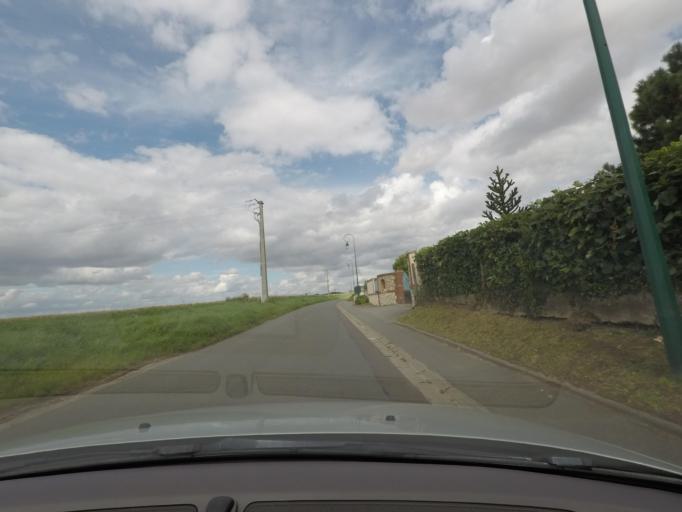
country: FR
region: Haute-Normandie
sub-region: Departement de l'Eure
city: Les Andelys
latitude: 49.1968
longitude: 1.4648
